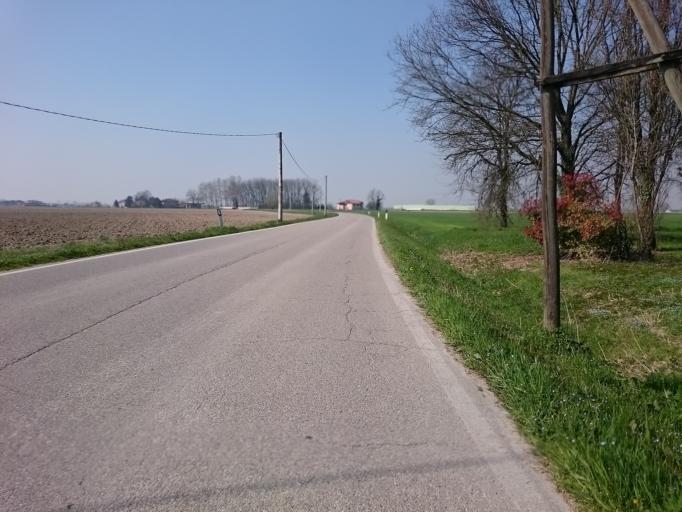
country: IT
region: Veneto
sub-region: Provincia di Padova
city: Carceri
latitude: 45.2020
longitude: 11.6399
